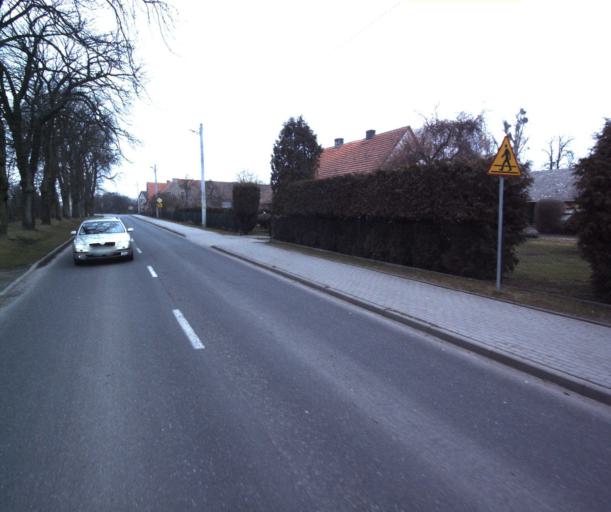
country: PL
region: West Pomeranian Voivodeship
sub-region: Powiat gryfinski
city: Mieszkowice
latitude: 52.8029
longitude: 14.5683
